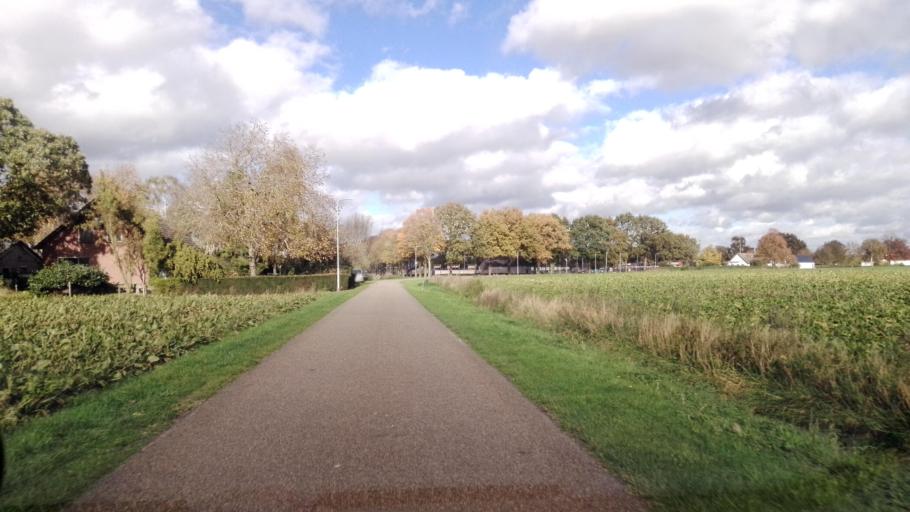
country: NL
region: Limburg
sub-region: Gemeente Venray
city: Venray
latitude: 51.4967
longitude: 6.0393
